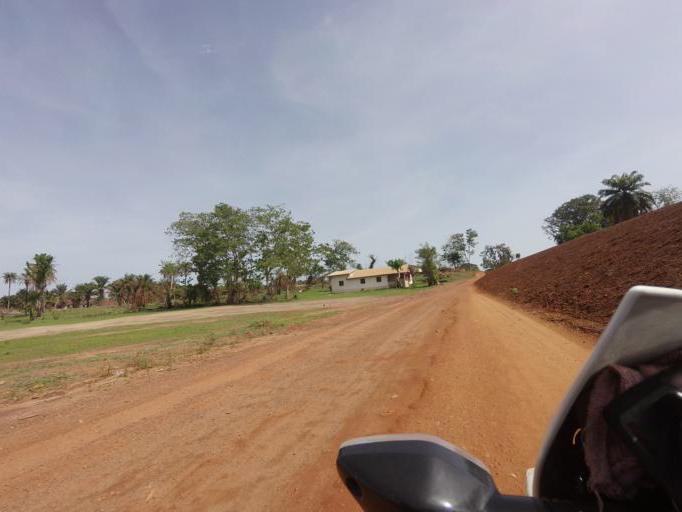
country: SL
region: Northern Province
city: Makeni
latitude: 9.1040
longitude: -12.2070
